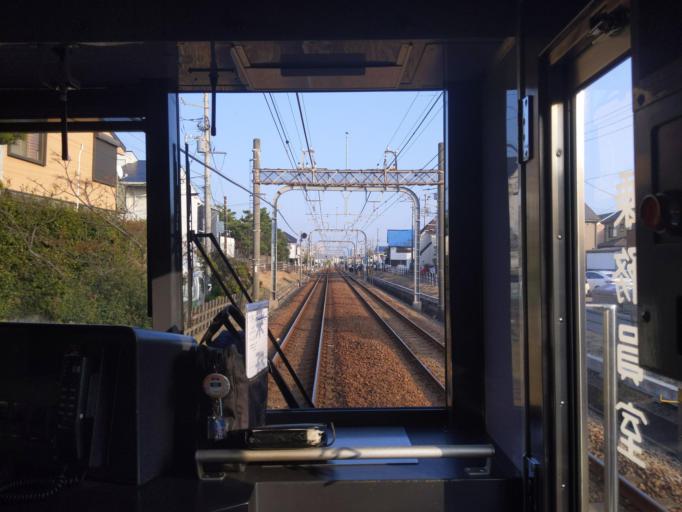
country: JP
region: Kanagawa
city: Fujisawa
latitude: 35.3170
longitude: 139.4747
